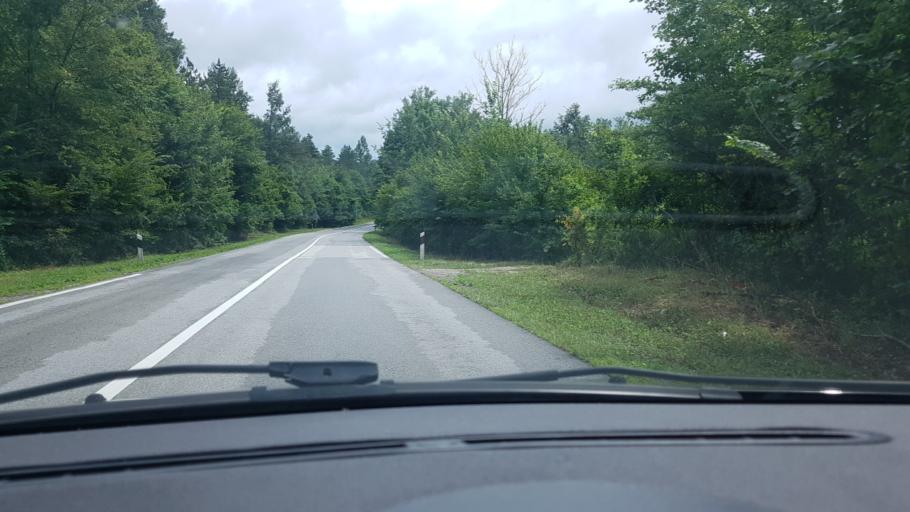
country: HR
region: Licko-Senjska
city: Jezerce
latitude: 44.9315
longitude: 15.6987
